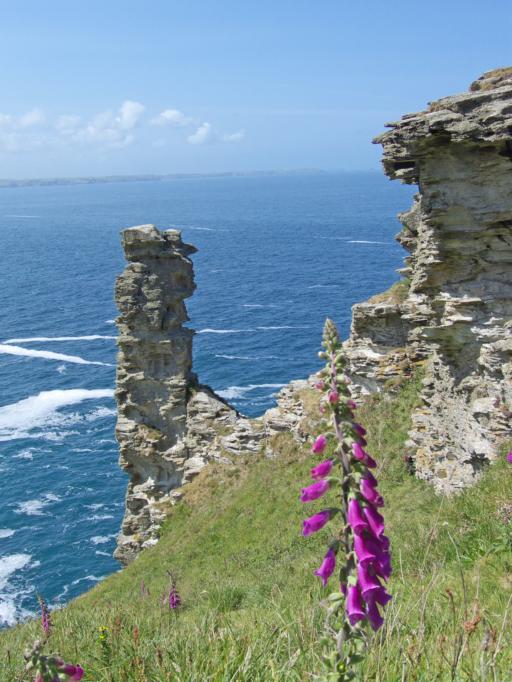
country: GB
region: England
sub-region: Cornwall
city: Tintagel
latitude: 50.6695
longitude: -4.7635
